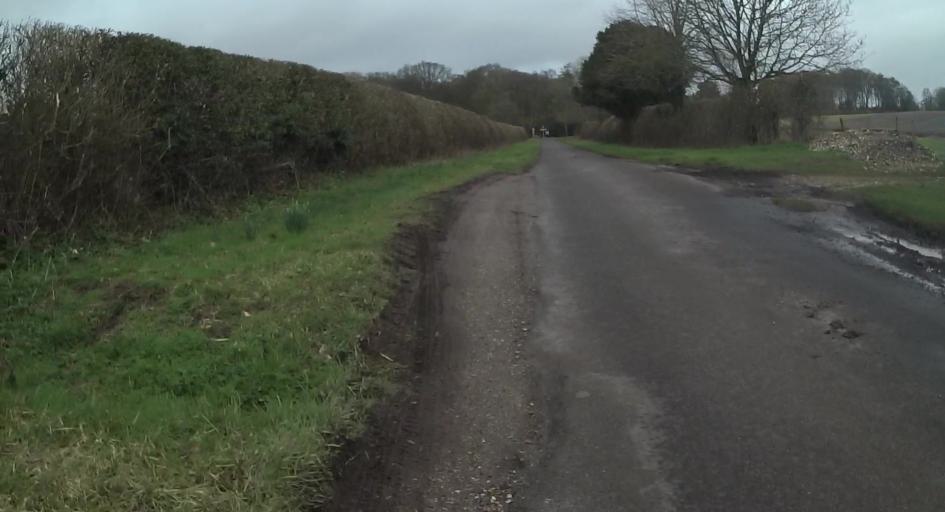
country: GB
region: England
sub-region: Hampshire
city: Kingsclere
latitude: 51.2730
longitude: -1.2008
